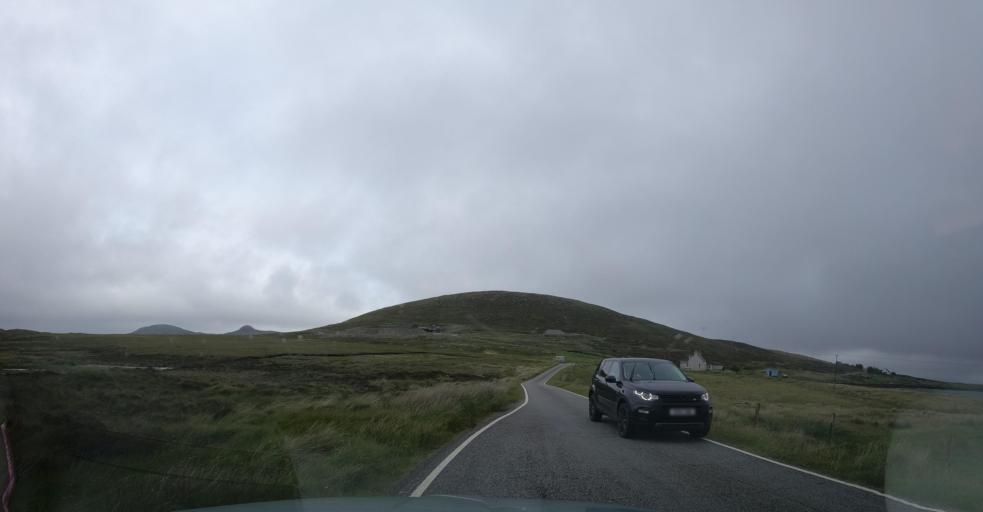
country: GB
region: Scotland
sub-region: Eilean Siar
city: Isle of North Uist
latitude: 57.6200
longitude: -7.2045
